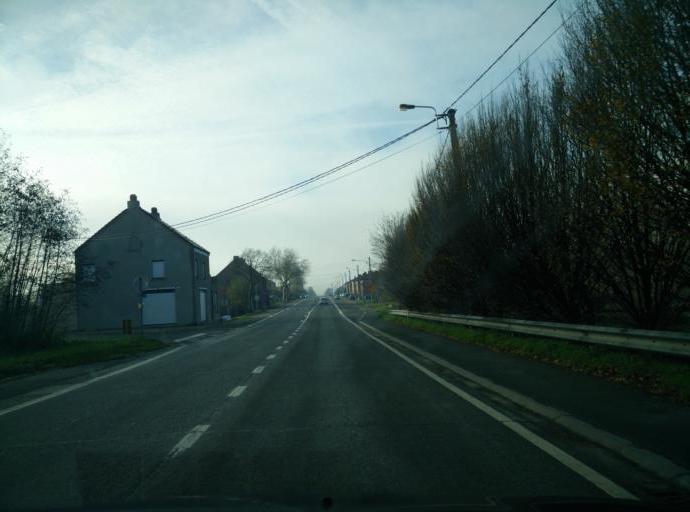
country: BE
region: Wallonia
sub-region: Province du Brabant Wallon
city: Rebecq-Rognon
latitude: 50.6917
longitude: 4.1003
